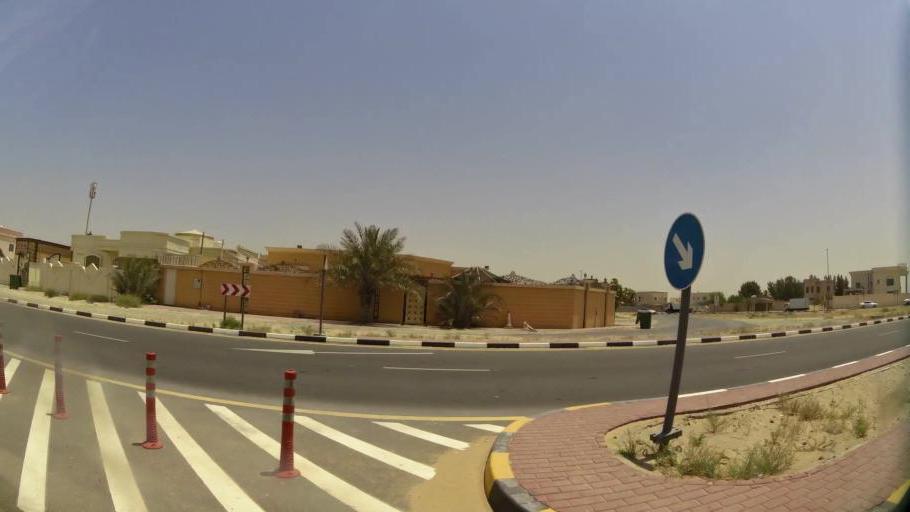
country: AE
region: Ajman
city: Ajman
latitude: 25.4067
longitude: 55.5242
